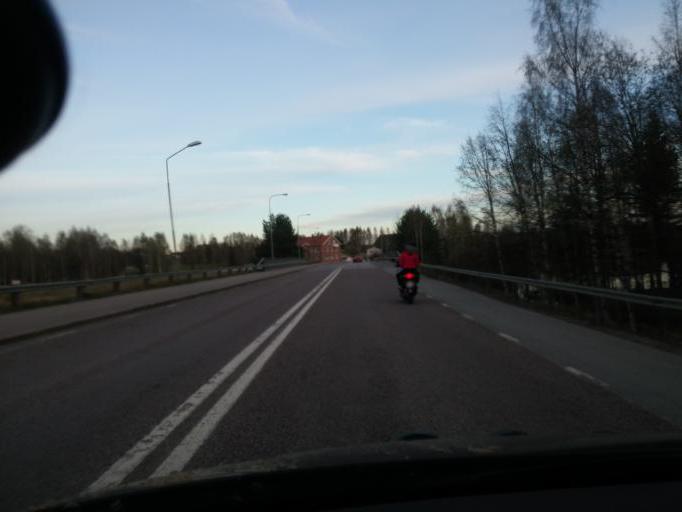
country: SE
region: Gaevleborg
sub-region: Ljusdals Kommun
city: Ljusdal
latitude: 61.8346
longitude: 16.0672
